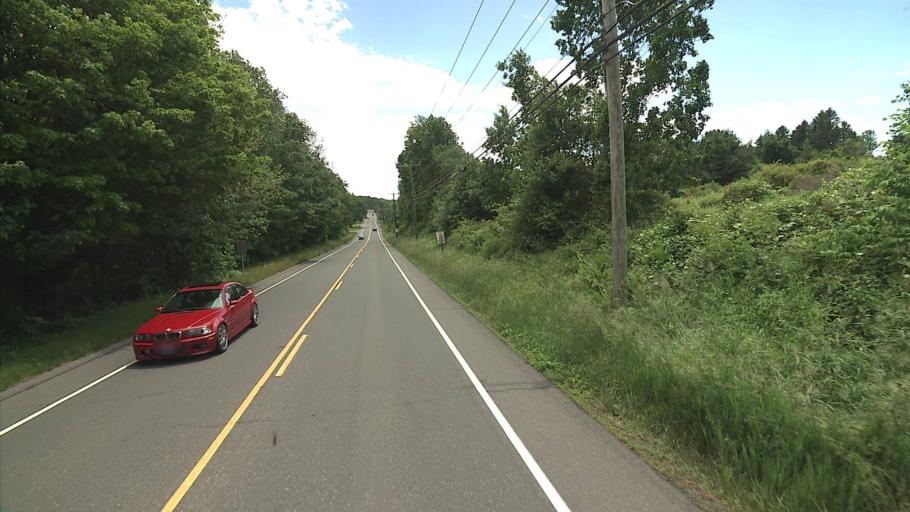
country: US
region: Connecticut
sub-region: Litchfield County
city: Watertown
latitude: 41.6353
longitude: -73.1413
